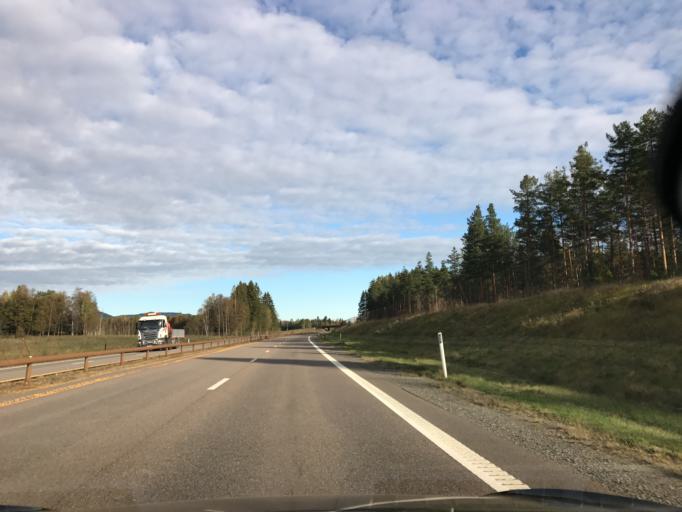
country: NO
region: Akershus
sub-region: Eidsvoll
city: Eidsvoll
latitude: 60.3644
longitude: 11.2041
